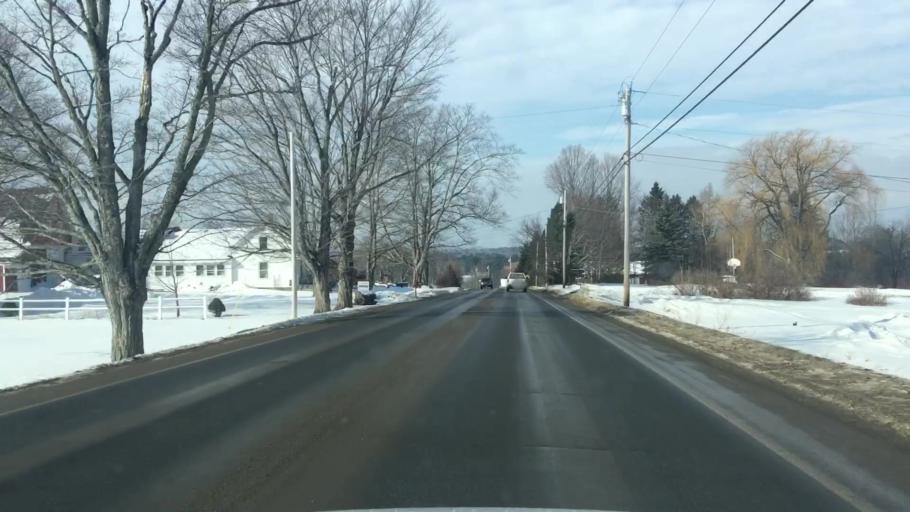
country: US
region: Maine
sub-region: Penobscot County
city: Hermon
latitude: 44.8472
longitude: -68.8719
